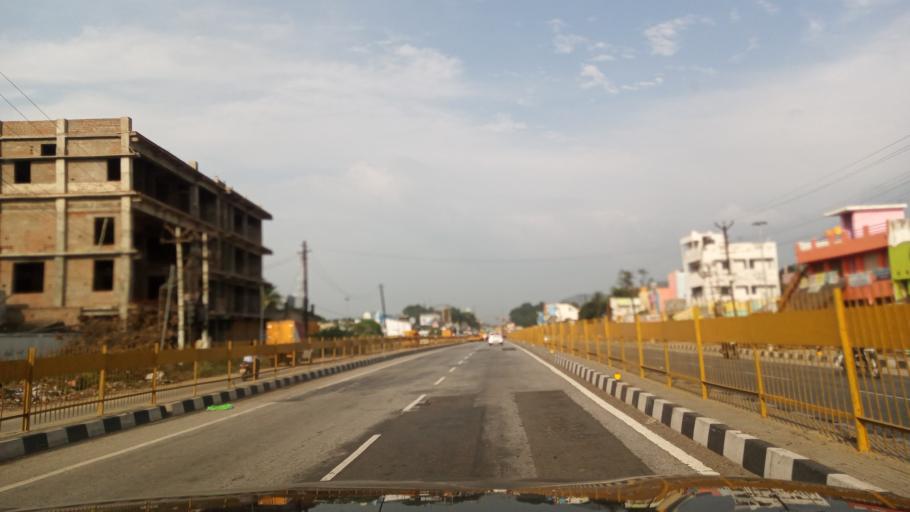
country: IN
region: Tamil Nadu
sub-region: Vellore
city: Ambur
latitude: 12.7783
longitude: 78.7163
